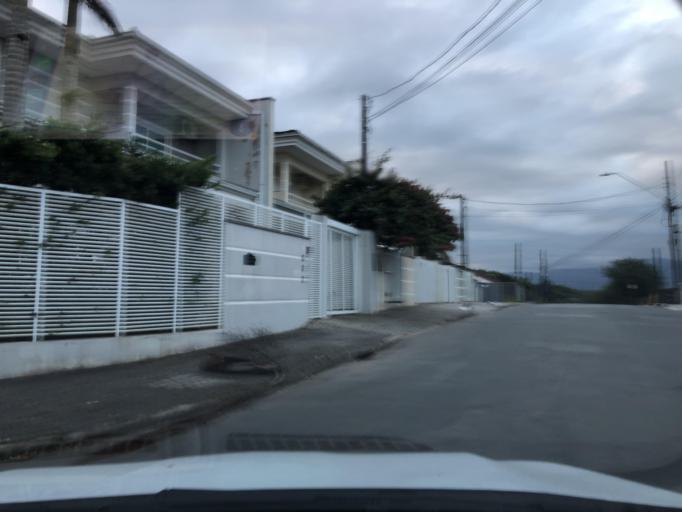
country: BR
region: Santa Catarina
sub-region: Joinville
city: Joinville
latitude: -26.2886
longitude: -48.8779
